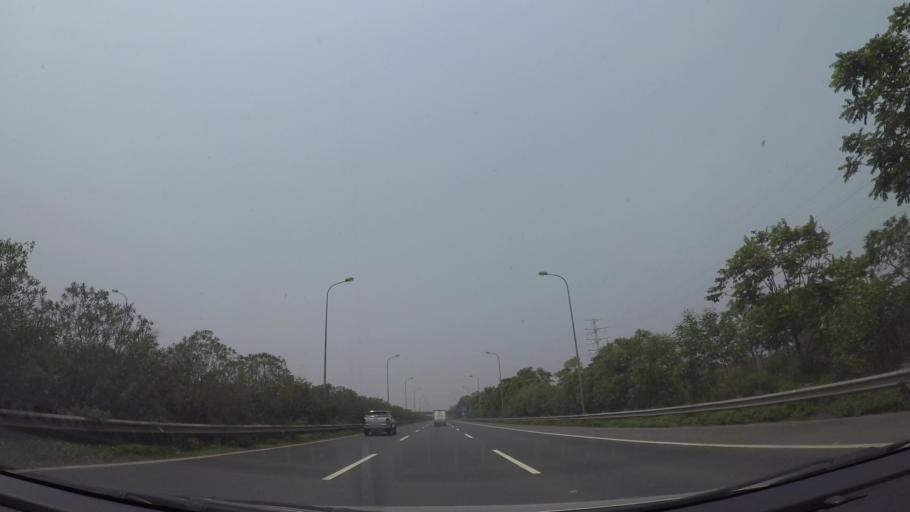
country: VN
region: Ha Noi
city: Lien Quan
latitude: 20.9906
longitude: 105.5396
